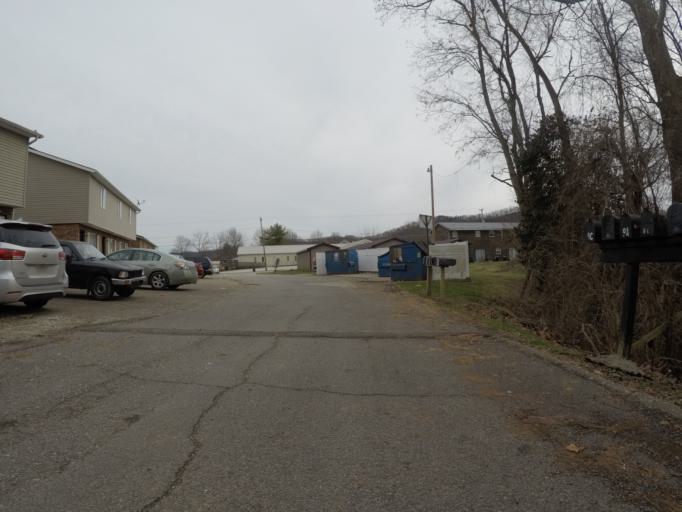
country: US
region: West Virginia
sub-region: Cabell County
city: Pea Ridge
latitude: 38.4439
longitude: -82.3415
